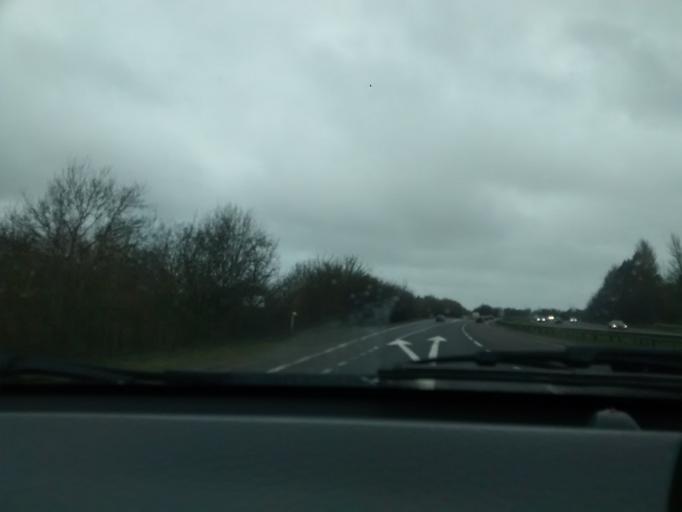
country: GB
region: England
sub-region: Suffolk
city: Bramford
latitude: 52.0987
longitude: 1.1120
